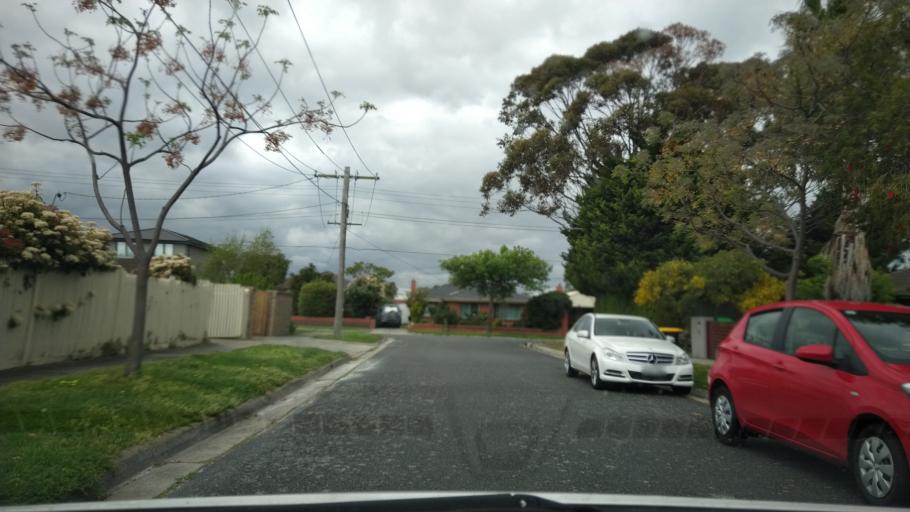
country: AU
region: Victoria
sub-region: Kingston
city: Mentone
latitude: -37.9675
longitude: 145.0796
